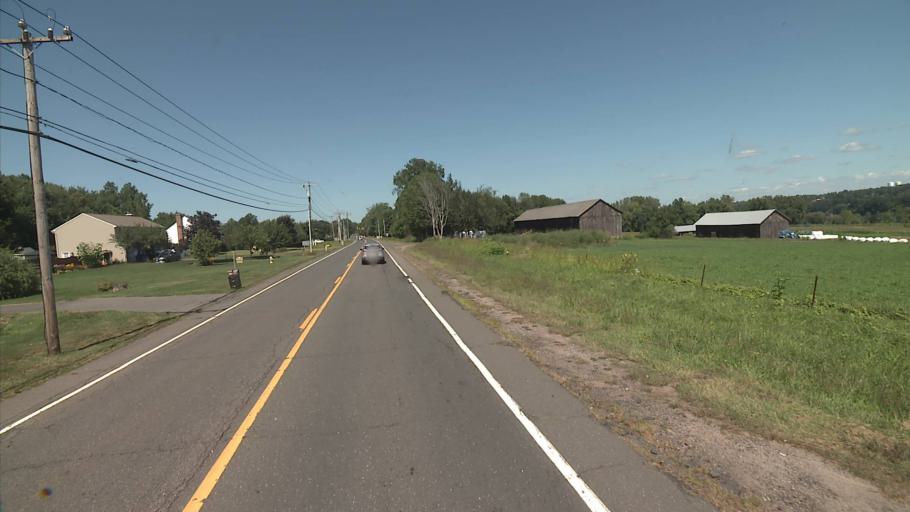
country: US
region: Connecticut
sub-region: Hartford County
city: Enfield
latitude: 41.9796
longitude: -72.6136
